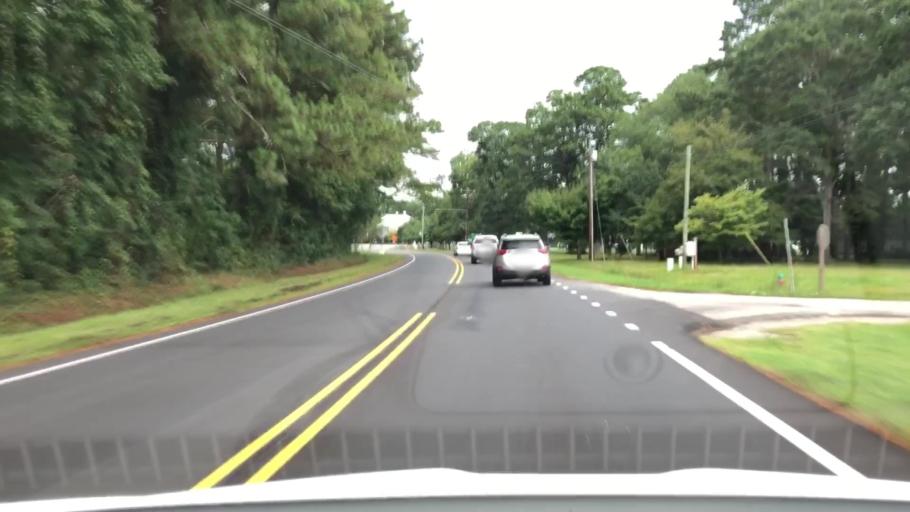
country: US
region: North Carolina
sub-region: Jones County
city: Maysville
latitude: 34.9013
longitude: -77.2259
